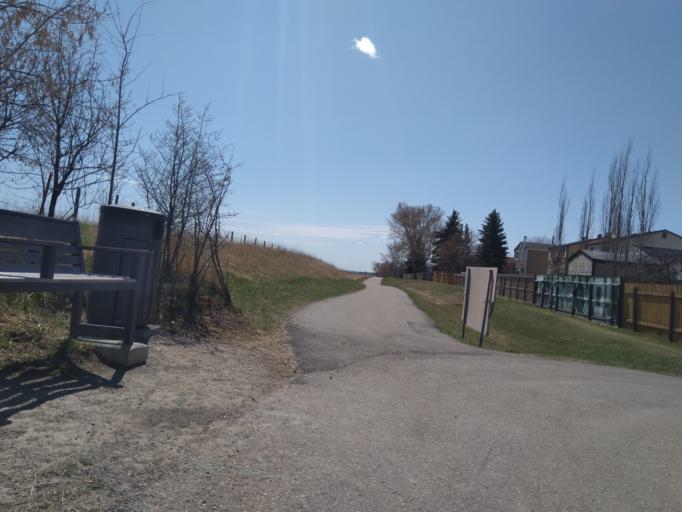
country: CA
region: Alberta
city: Chestermere
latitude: 51.0625
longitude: -113.9234
